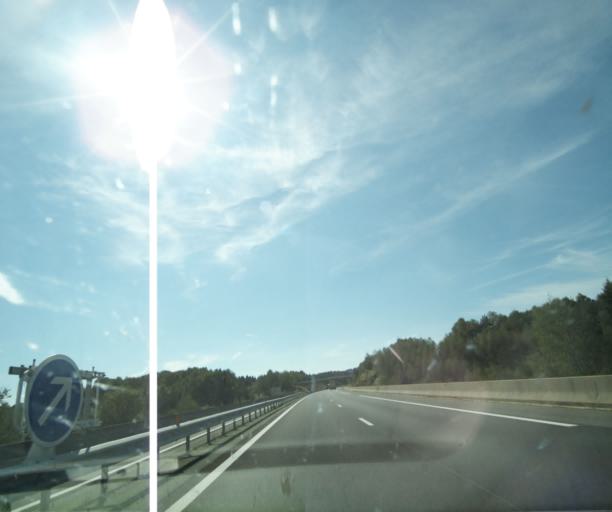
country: FR
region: Limousin
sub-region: Departement de la Correze
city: Ussel
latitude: 45.5914
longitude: 2.4269
